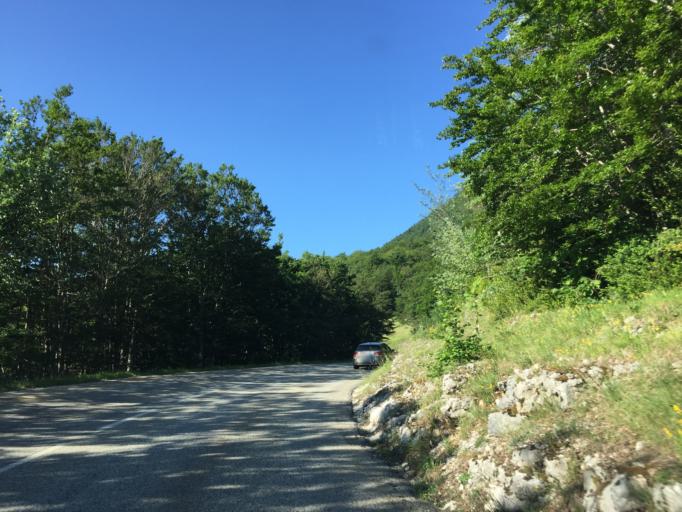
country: FR
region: Rhone-Alpes
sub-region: Departement de la Drome
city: Saint-Laurent-en-Royans
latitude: 44.9373
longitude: 5.3839
